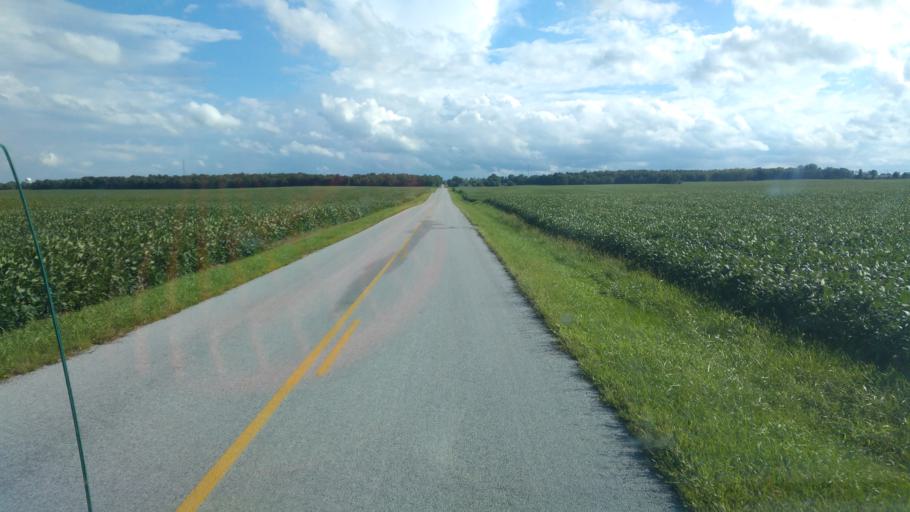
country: US
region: Ohio
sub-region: Hardin County
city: Kenton
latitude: 40.6807
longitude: -83.6336
